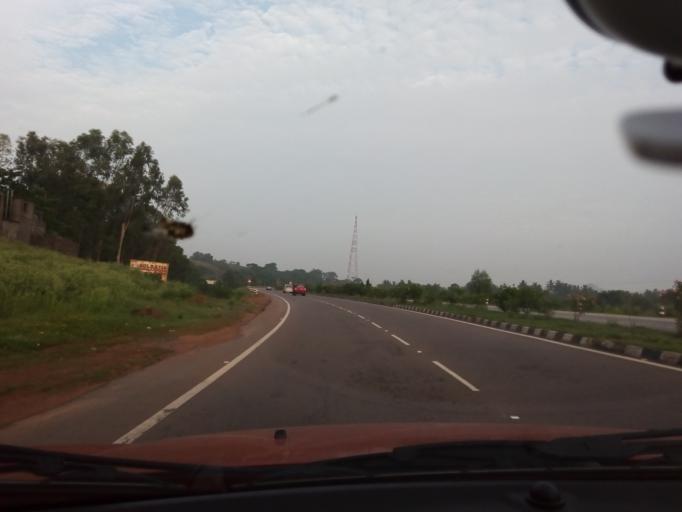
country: IN
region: Karnataka
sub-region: Ramanagara
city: Magadi
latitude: 13.0734
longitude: 77.2239
